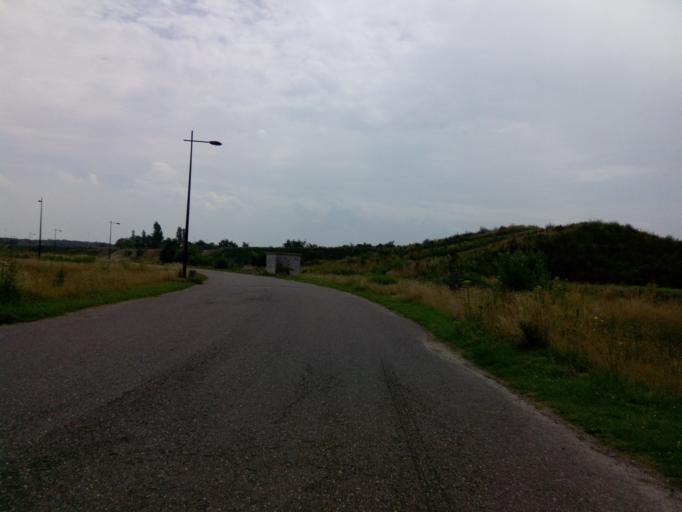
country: NL
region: Utrecht
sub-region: Gemeente Amersfoort
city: Randenbroek
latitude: 52.1800
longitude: 5.4247
